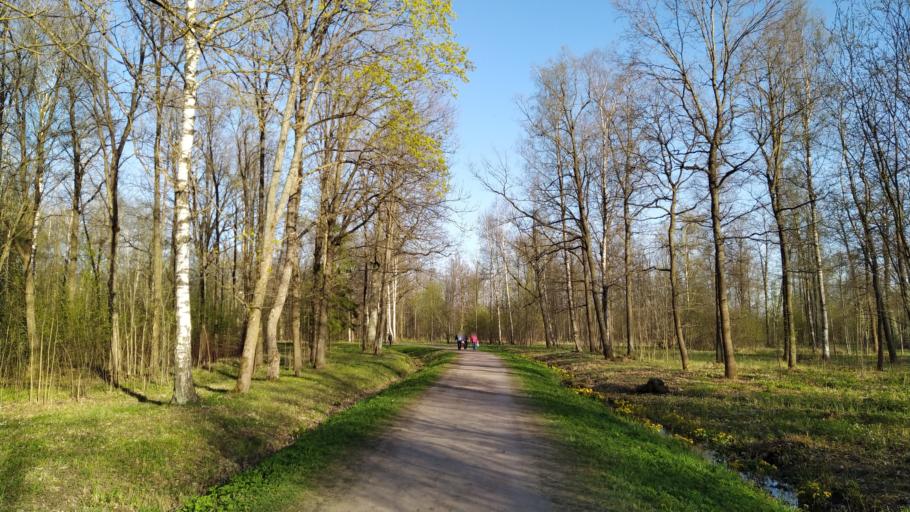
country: RU
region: St.-Petersburg
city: Aleksandrovskaya
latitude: 59.7056
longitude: 30.3500
